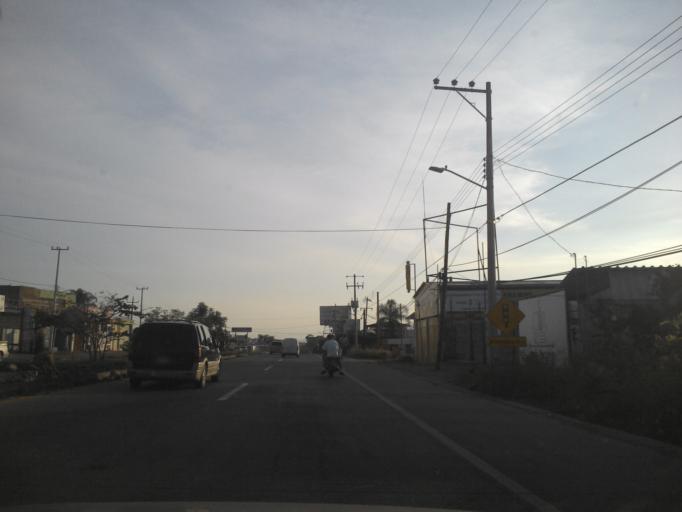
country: MX
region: Jalisco
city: Zapotlanejo
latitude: 20.6134
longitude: -103.0826
